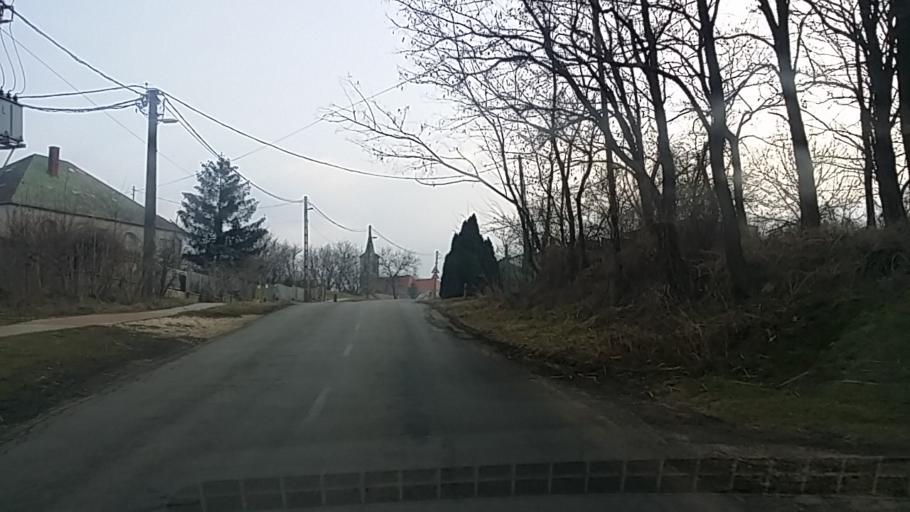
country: HU
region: Komarom-Esztergom
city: Bokod
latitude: 47.5218
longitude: 18.2254
